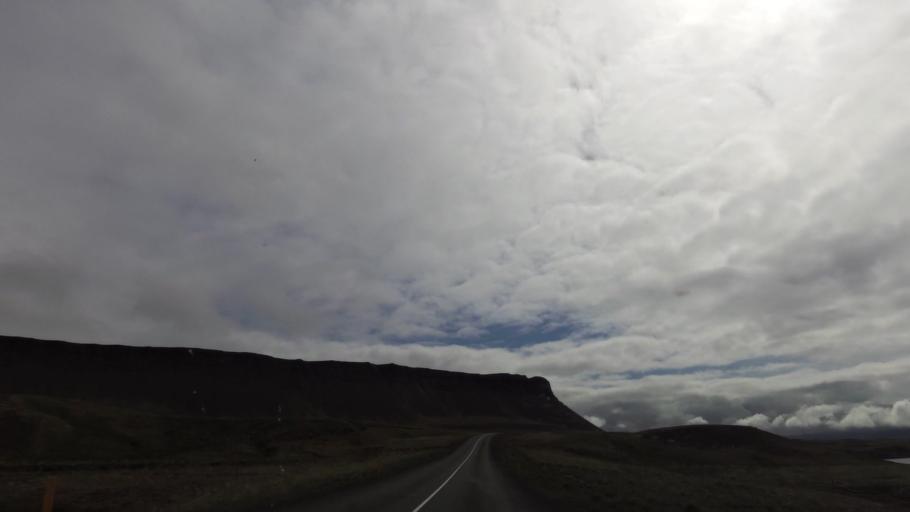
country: IS
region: West
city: Stykkisholmur
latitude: 65.4706
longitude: -21.9165
